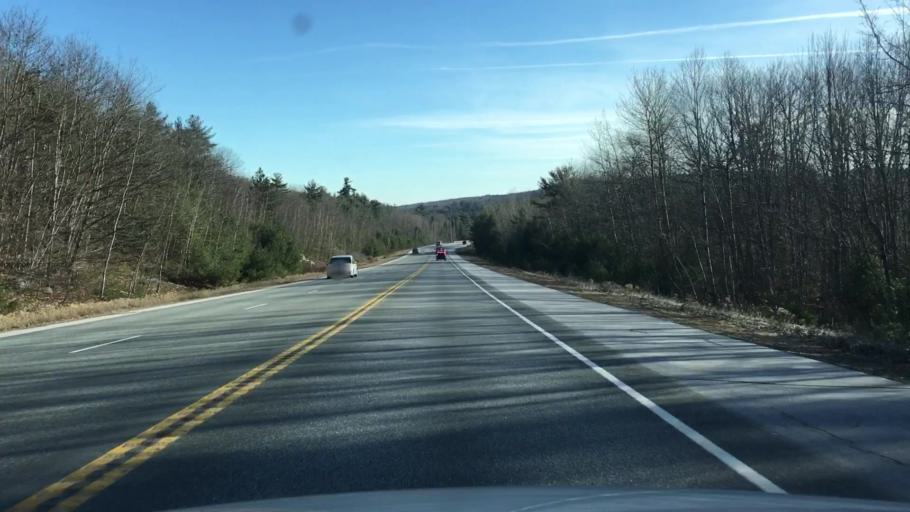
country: US
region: Maine
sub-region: Hancock County
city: Dedham
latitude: 44.6855
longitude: -68.5816
